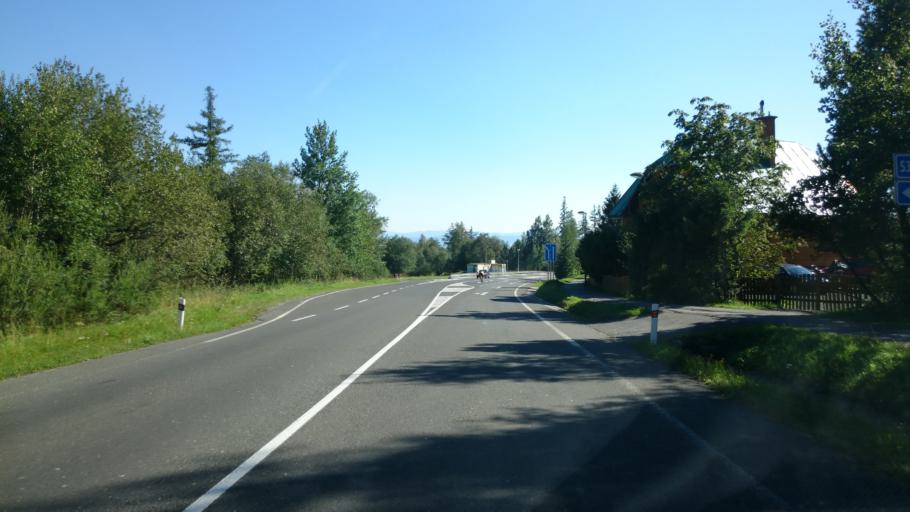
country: SK
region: Presovsky
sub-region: Okres Poprad
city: Nova Lesna
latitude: 49.1739
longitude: 20.2941
